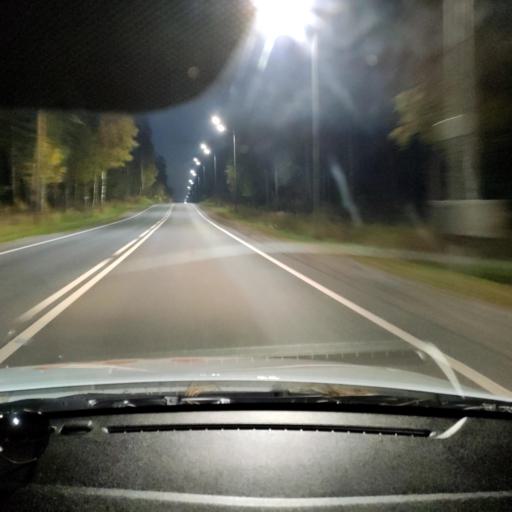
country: RU
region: Tatarstan
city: Stolbishchi
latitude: 55.6342
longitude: 49.0874
